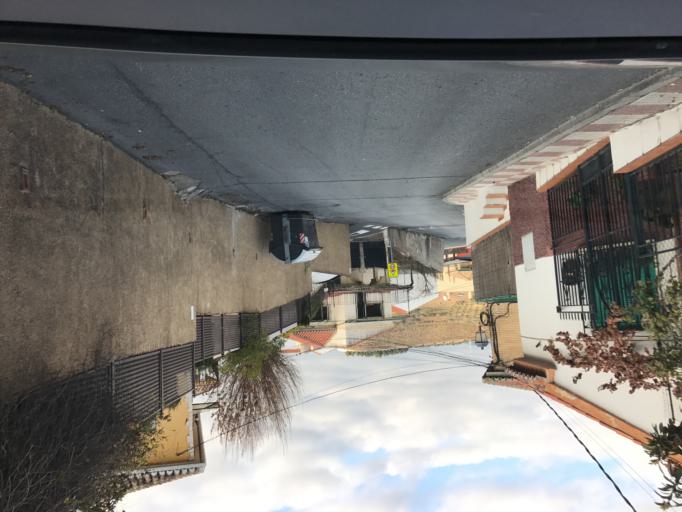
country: ES
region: Andalusia
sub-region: Provincia de Granada
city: Cajar
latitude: 37.1347
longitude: -3.5568
